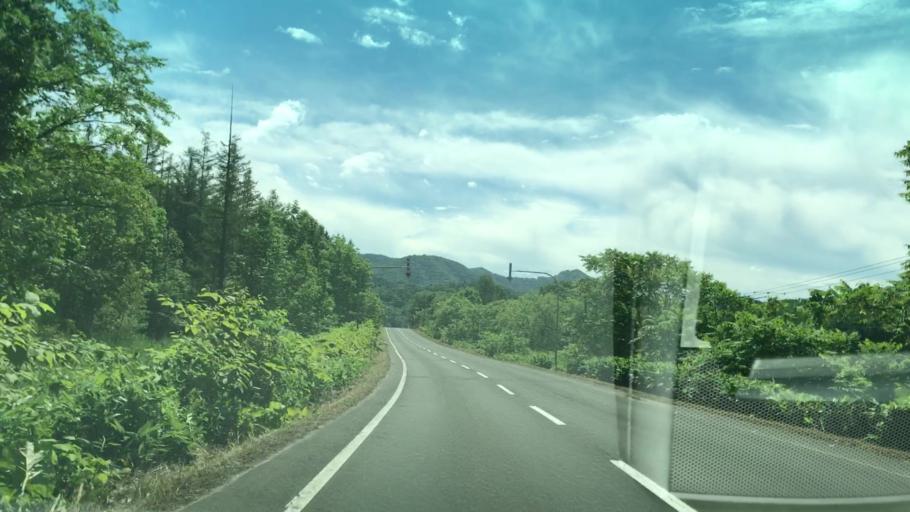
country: JP
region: Hokkaido
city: Shimo-furano
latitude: 42.9551
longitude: 142.4316
